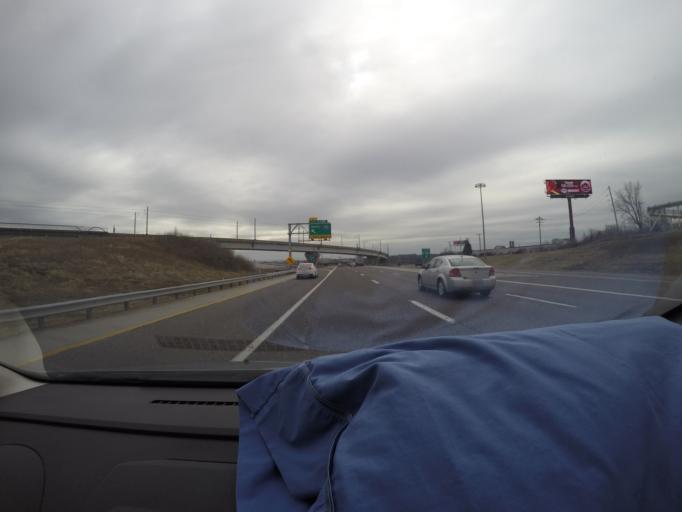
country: US
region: Missouri
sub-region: Saint Louis County
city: Saint Johns
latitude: 38.7304
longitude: -90.3353
